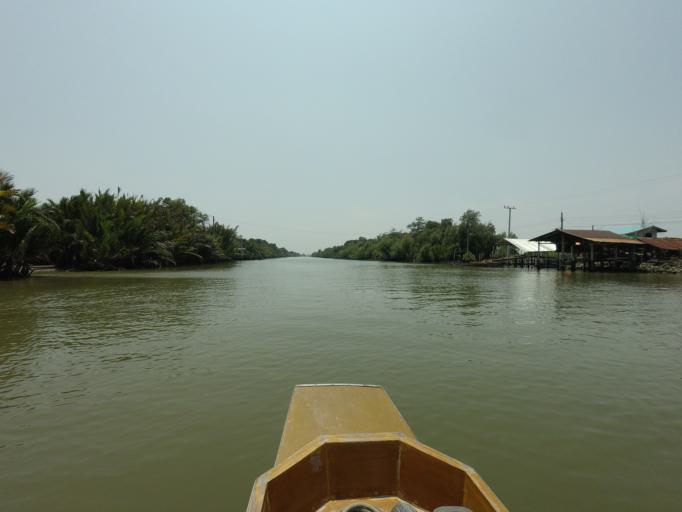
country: TH
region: Bangkok
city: Thung Khru
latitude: 13.5430
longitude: 100.4628
